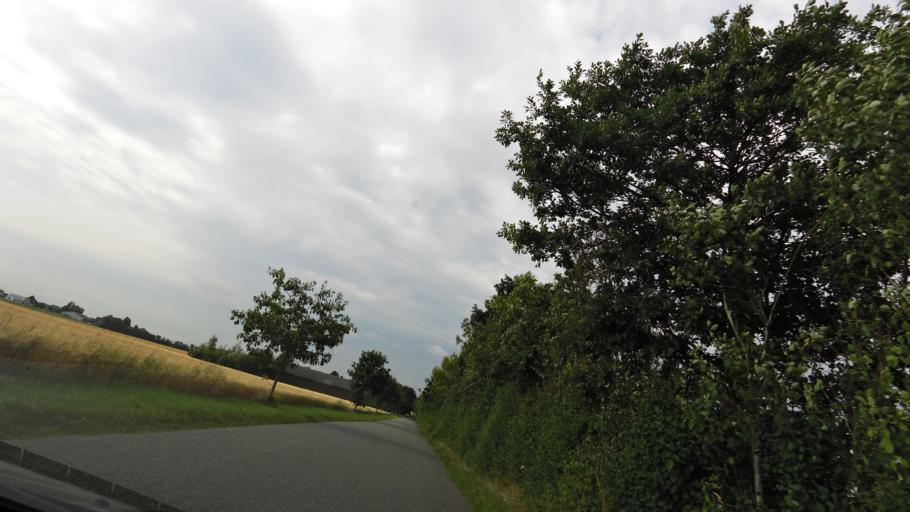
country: DK
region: South Denmark
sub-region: Nordfyns Kommune
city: Otterup
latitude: 55.5601
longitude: 10.4228
